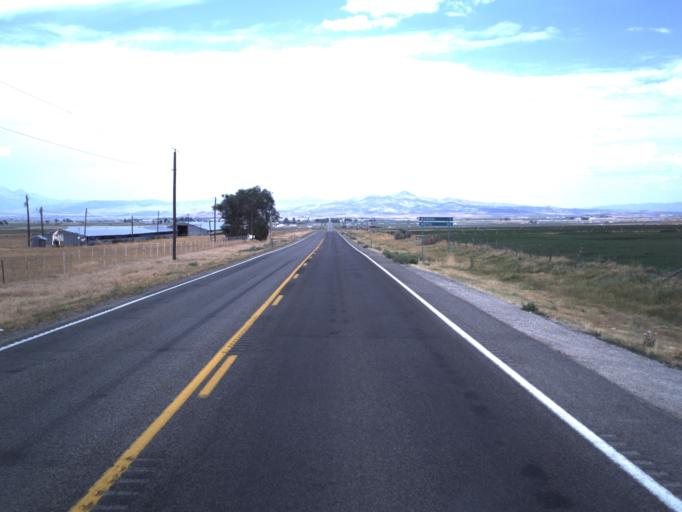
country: US
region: Utah
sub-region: Sanpete County
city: Ephraim
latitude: 39.4250
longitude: -111.5622
